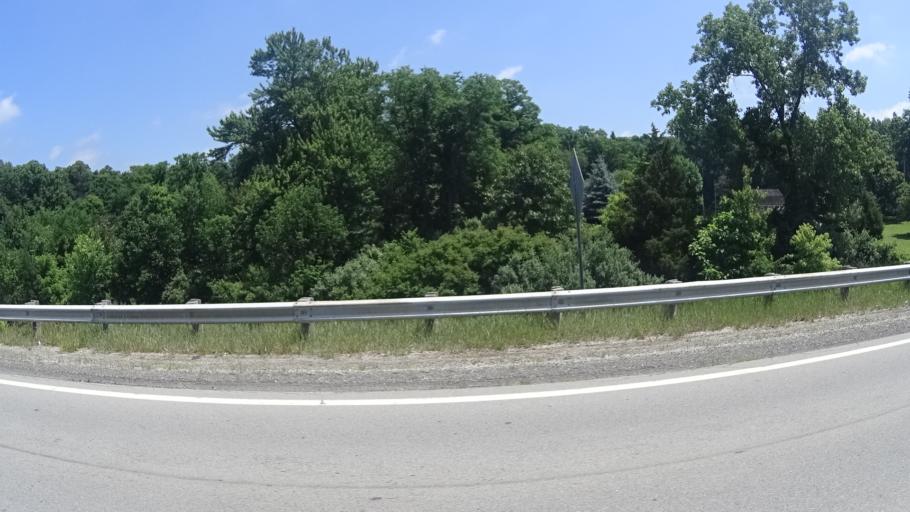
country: US
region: Ohio
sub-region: Lorain County
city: Vermilion
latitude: 41.3363
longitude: -82.3602
